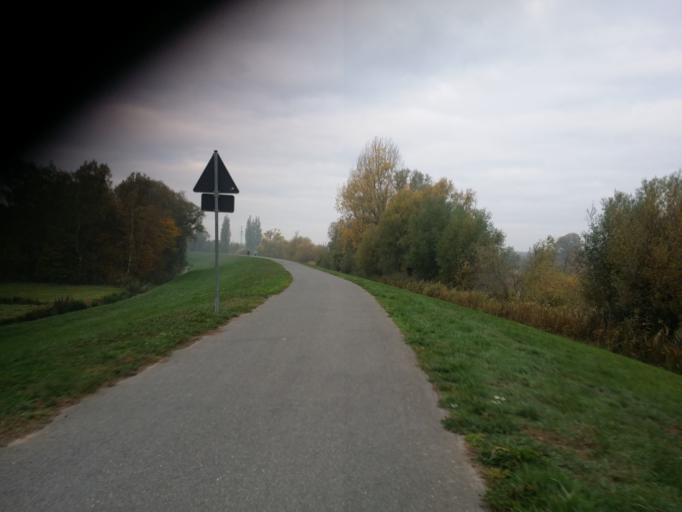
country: DE
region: Lower Saxony
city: Ritterhude
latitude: 53.1627
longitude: 8.7177
